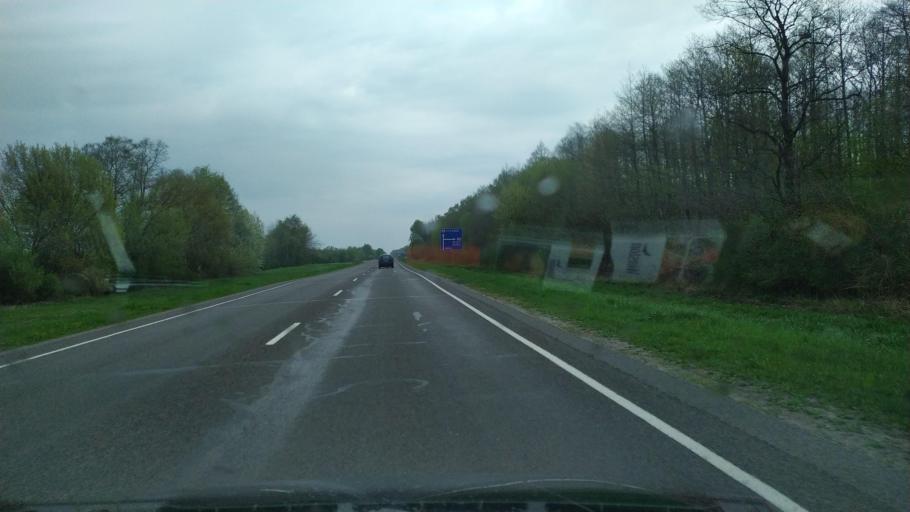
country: BY
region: Brest
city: Horad Kobryn
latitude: 52.3219
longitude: 24.5622
